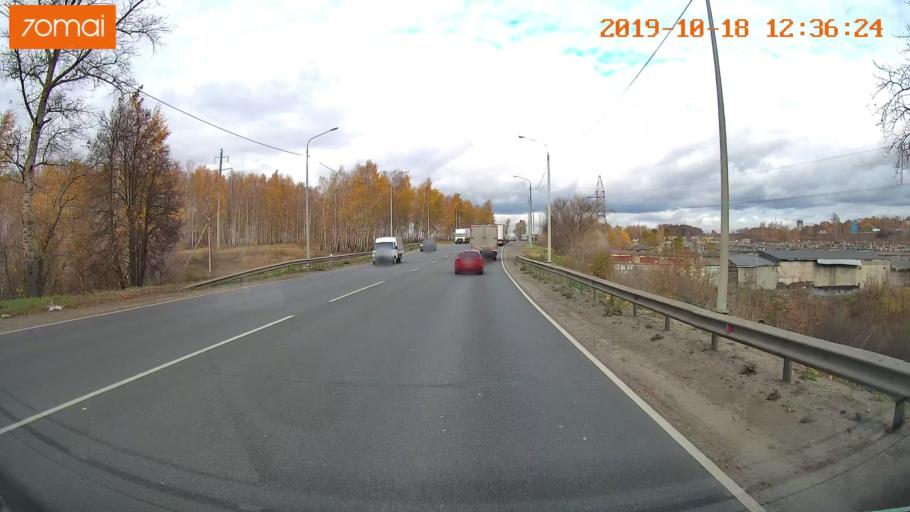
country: RU
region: Rjazan
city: Ryazan'
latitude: 54.6345
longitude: 39.6335
